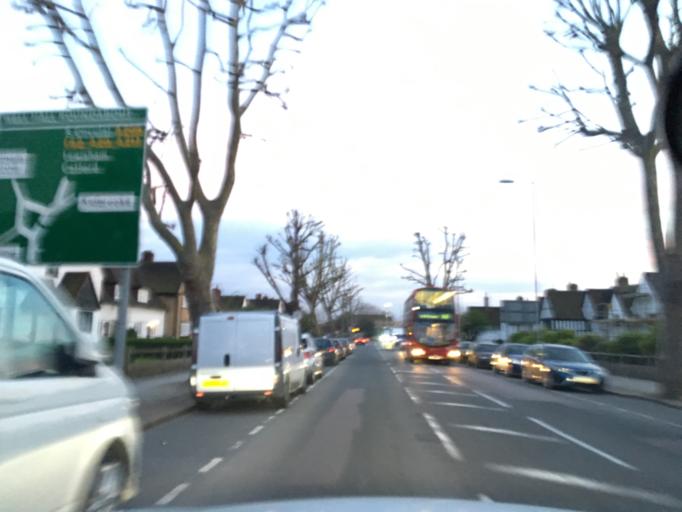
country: GB
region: England
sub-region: Greater London
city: Woolwich
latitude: 51.4625
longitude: 0.0502
